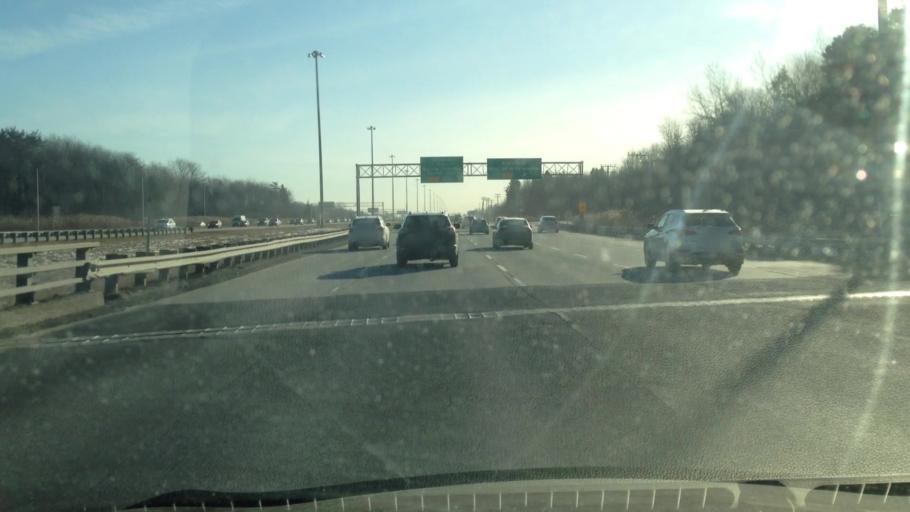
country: CA
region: Quebec
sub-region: Laurentides
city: Blainville
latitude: 45.6578
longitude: -73.8854
